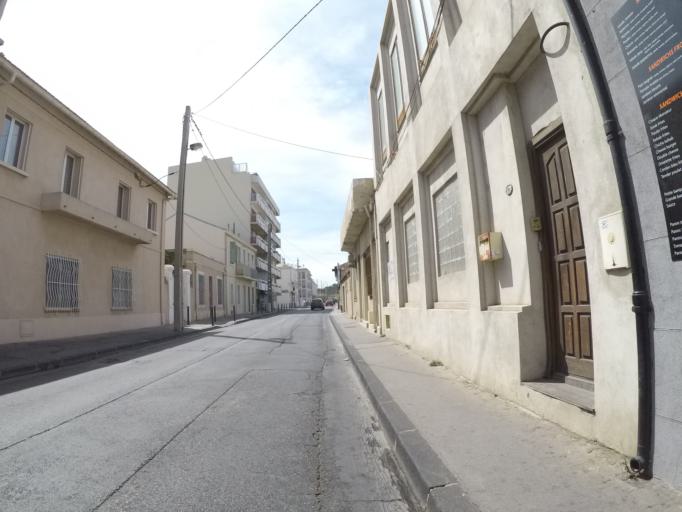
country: FR
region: Provence-Alpes-Cote d'Azur
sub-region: Departement des Bouches-du-Rhone
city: Marseille 08
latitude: 43.2360
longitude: 5.3616
